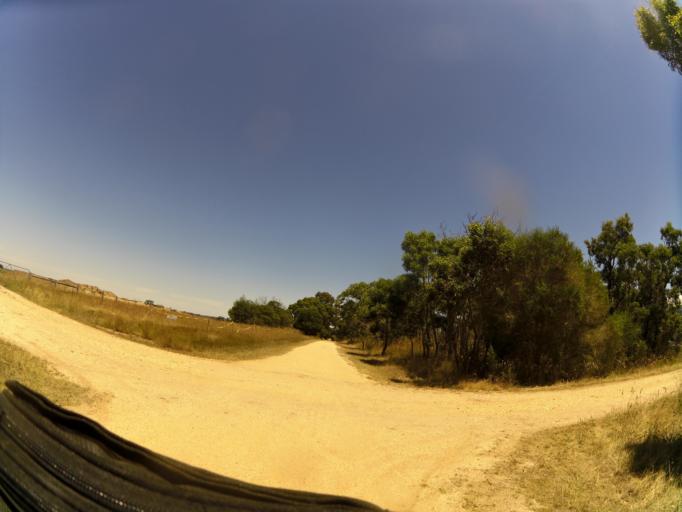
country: AU
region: Victoria
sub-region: Wellington
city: Sale
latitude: -37.9737
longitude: 146.9995
